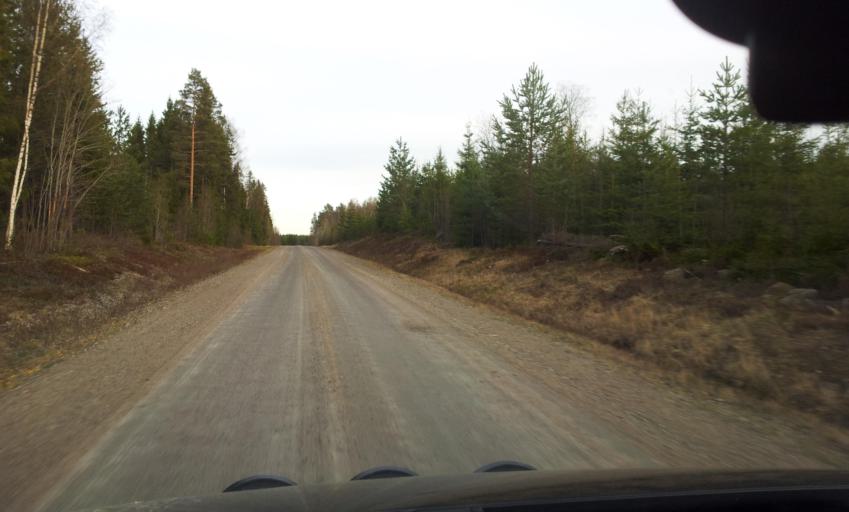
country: SE
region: Gaevleborg
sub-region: Ljusdals Kommun
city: Farila
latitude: 62.0887
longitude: 15.7643
